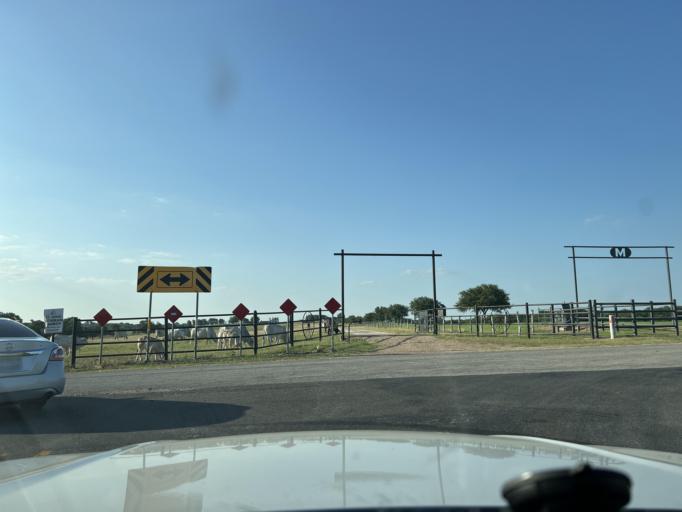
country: US
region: Texas
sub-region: Washington County
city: Brenham
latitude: 30.2295
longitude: -96.3918
